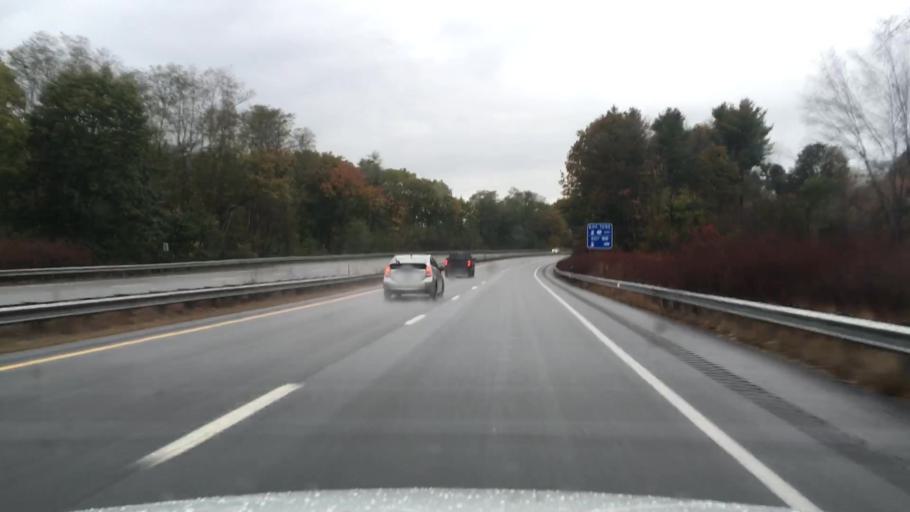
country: US
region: New Hampshire
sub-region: Strafford County
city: Dover
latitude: 43.1749
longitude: -70.8679
